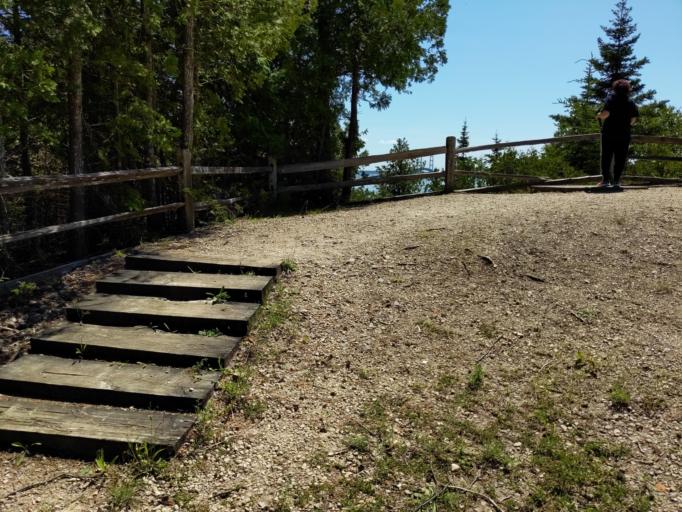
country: US
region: Michigan
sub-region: Mackinac County
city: Saint Ignace
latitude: 45.8512
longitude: -84.7265
